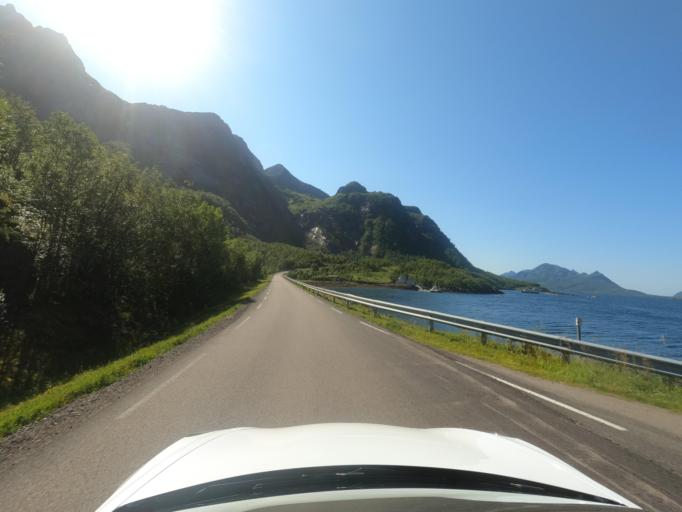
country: NO
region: Nordland
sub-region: Hadsel
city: Stokmarknes
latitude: 68.3452
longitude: 15.0509
